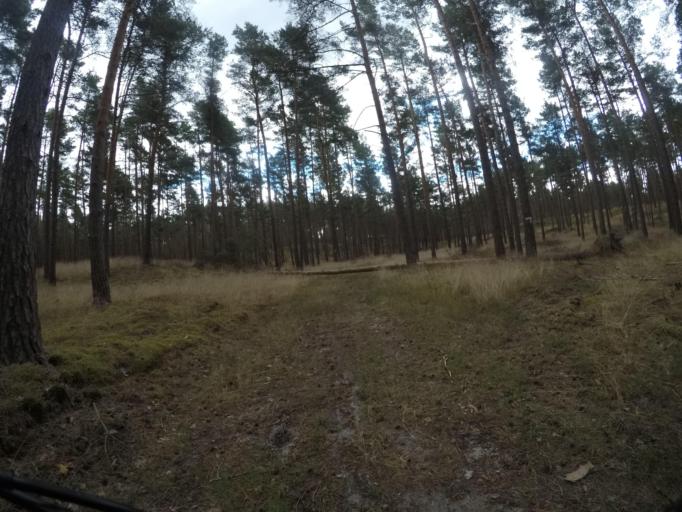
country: DE
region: Lower Saxony
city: Hitzacker
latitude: 53.1937
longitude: 11.0592
